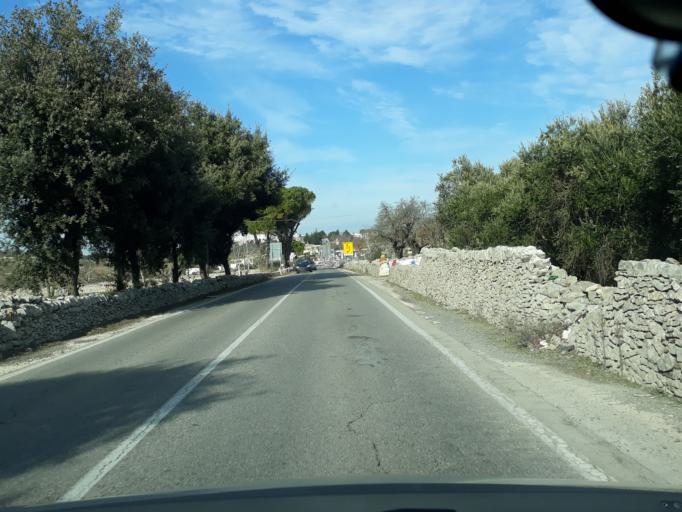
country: IT
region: Apulia
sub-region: Provincia di Bari
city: Locorotondo
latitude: 40.7328
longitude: 17.3326
